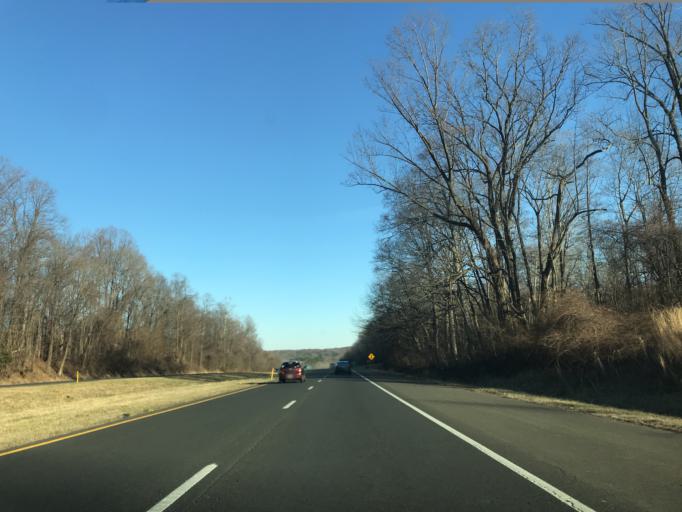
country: US
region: Maryland
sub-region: Prince George's County
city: Marlboro Meadows
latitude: 38.8124
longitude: -76.7214
